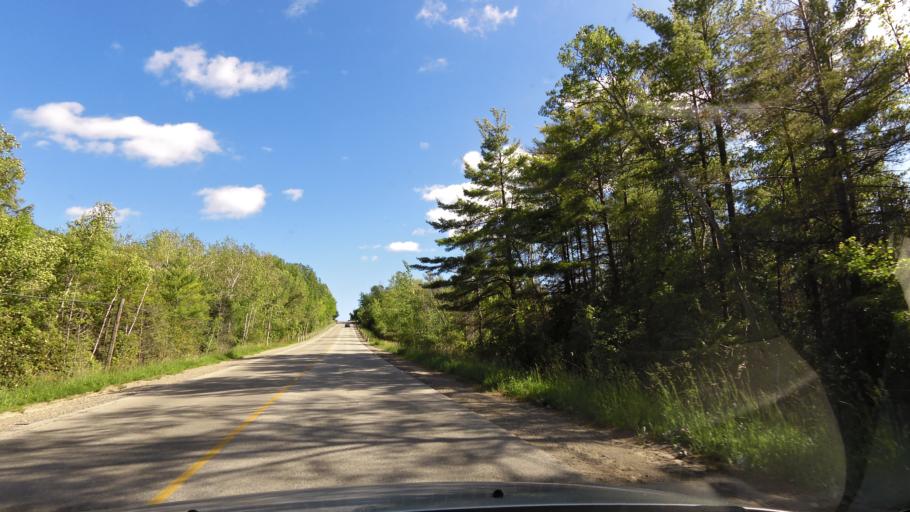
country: CA
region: Ontario
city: Bradford West Gwillimbury
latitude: 44.1701
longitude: -79.6177
